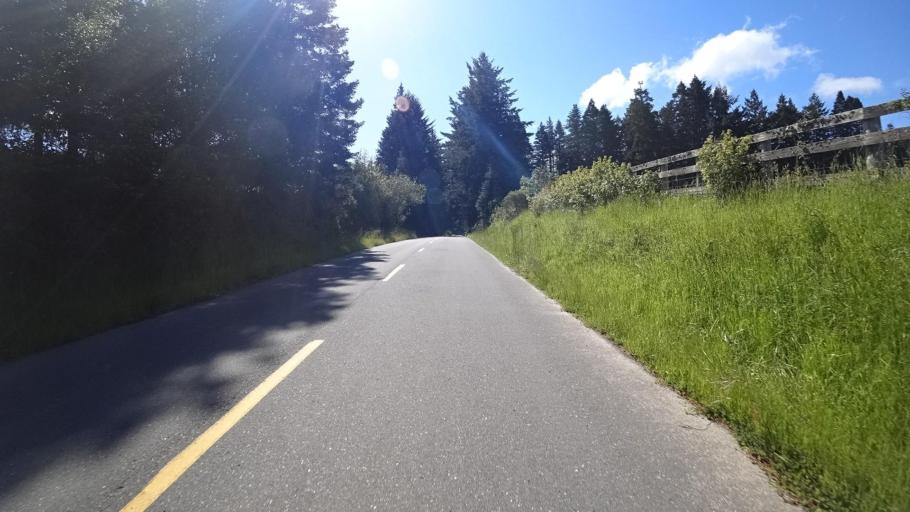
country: US
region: California
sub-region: Humboldt County
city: Ferndale
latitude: 40.3463
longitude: -124.3274
